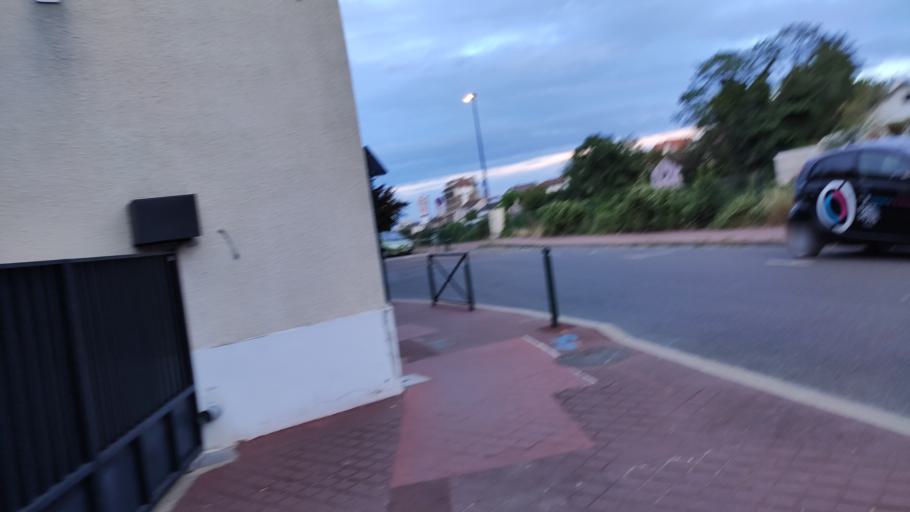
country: FR
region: Ile-de-France
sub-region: Departement des Hauts-de-Seine
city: Clamart
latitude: 48.8133
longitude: 2.2610
